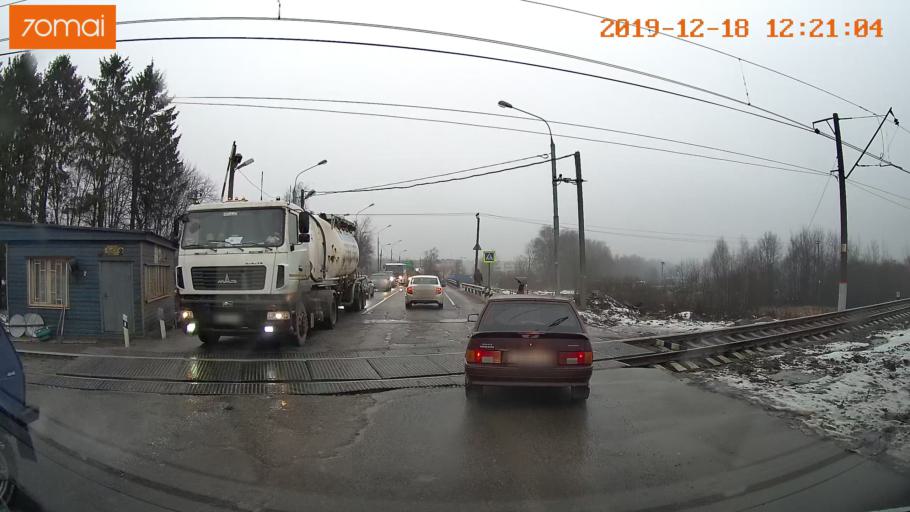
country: RU
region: Moskovskaya
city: Novopetrovskoye
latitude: 55.9970
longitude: 36.4744
